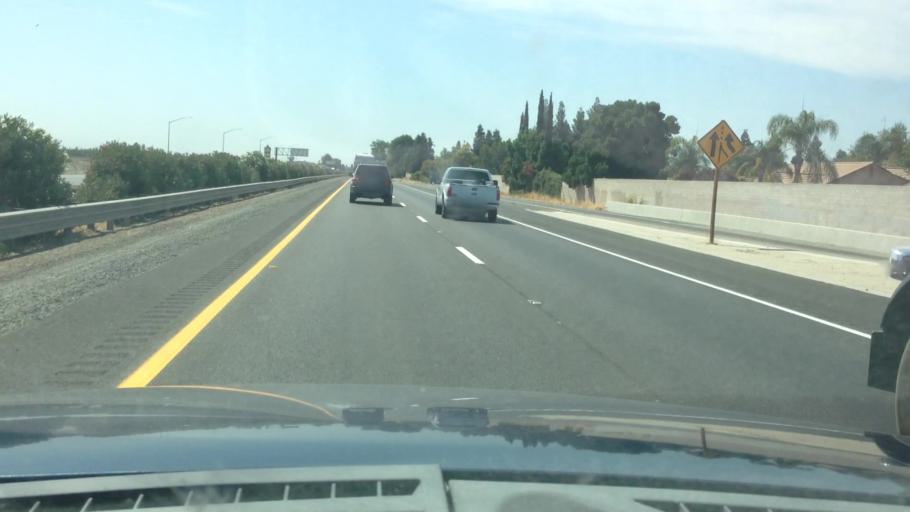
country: US
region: California
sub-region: Tulare County
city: Tulare
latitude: 36.2368
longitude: -119.3420
